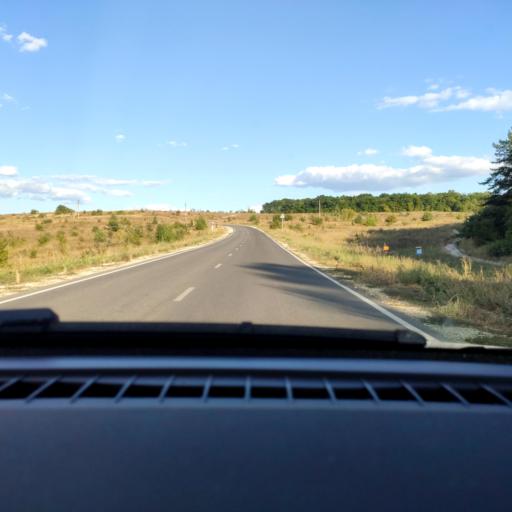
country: RU
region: Voronezj
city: Semiluki
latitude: 51.6569
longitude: 38.9965
